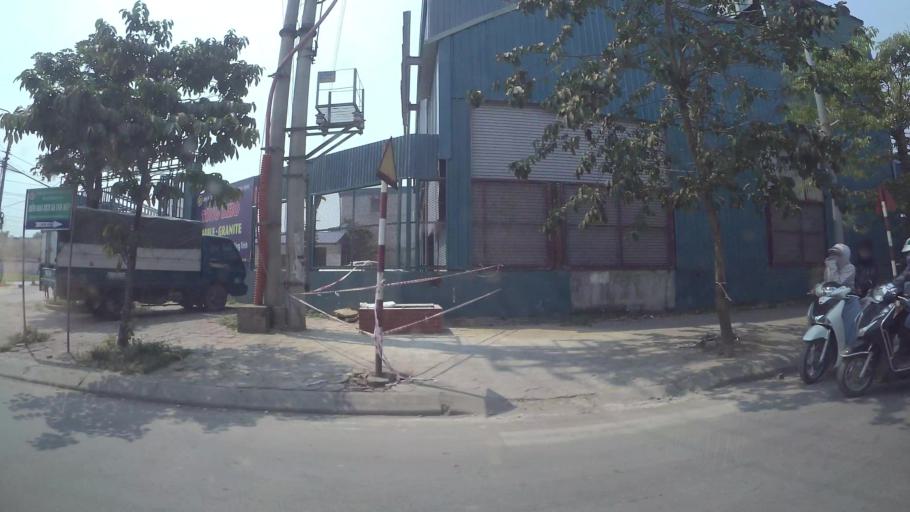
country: VN
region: Ha Noi
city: Van Dien
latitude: 20.9467
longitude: 105.8282
